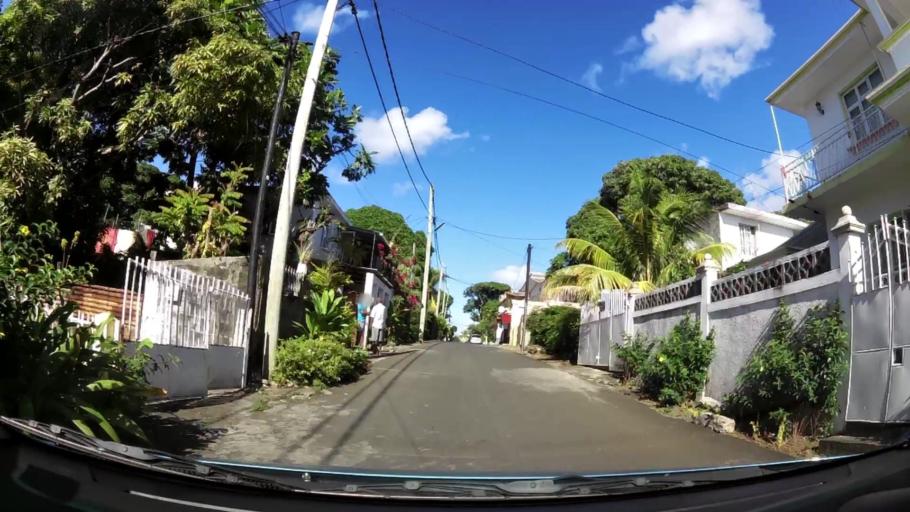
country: MU
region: Grand Port
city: Mahebourg
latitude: -20.4127
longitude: 57.7093
